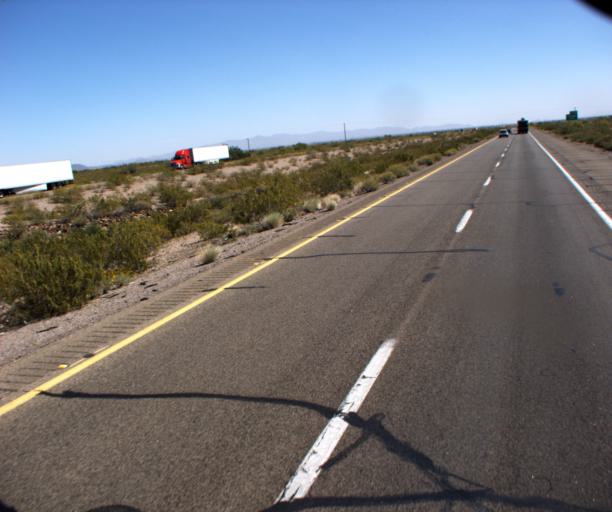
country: US
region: Arizona
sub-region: Maricopa County
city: Buckeye
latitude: 33.5043
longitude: -112.9753
